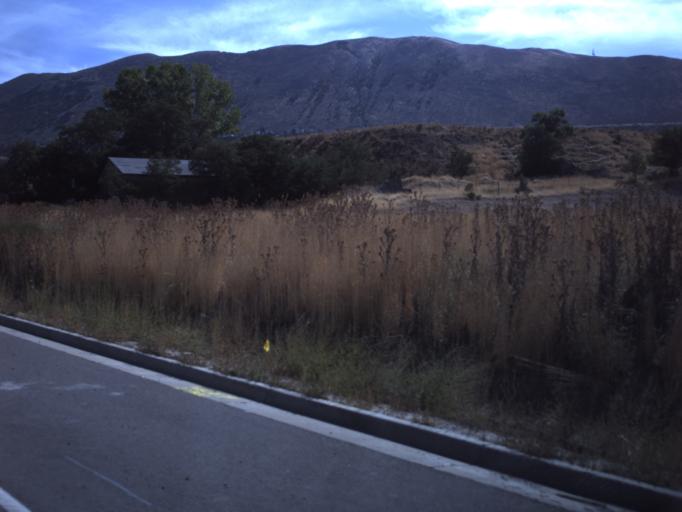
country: US
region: Utah
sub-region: Salt Lake County
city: Bluffdale
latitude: 40.4861
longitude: -111.9054
